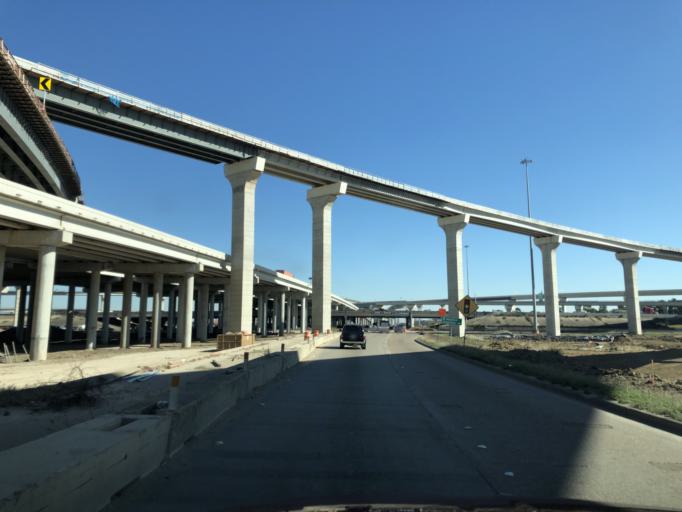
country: US
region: Texas
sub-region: Brazoria County
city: Brookside Village
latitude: 29.5967
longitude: -95.3896
